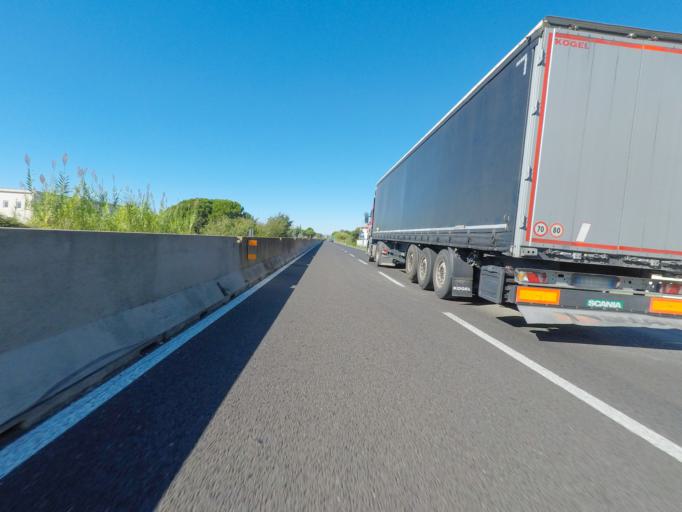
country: IT
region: Tuscany
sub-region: Provincia di Grosseto
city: Orbetello Scalo
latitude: 42.4647
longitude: 11.2419
